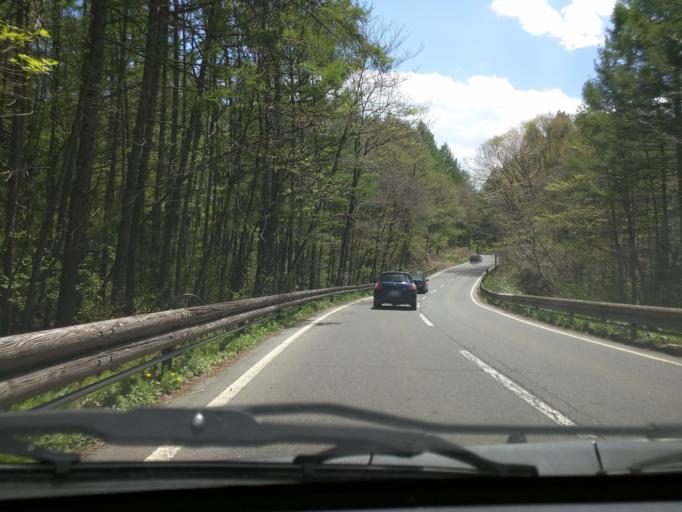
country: JP
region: Nagano
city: Nagano-shi
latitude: 36.7175
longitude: 138.1068
